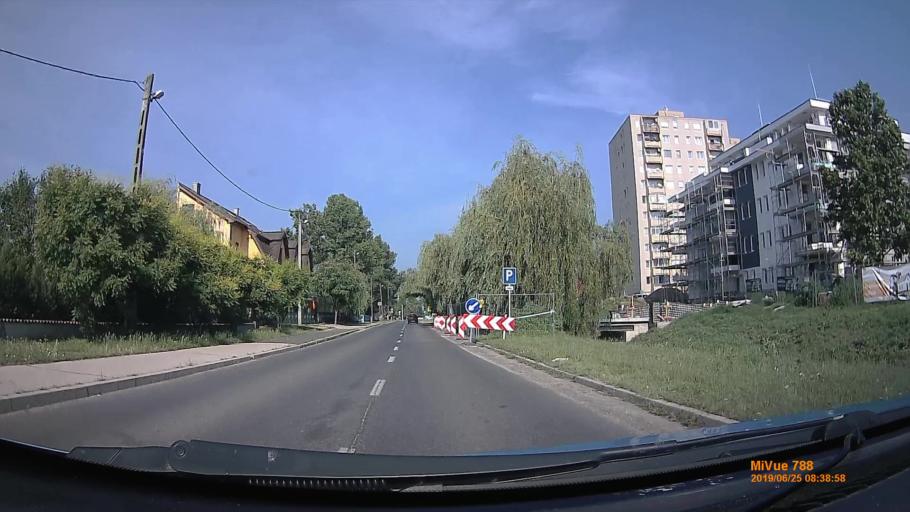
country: HU
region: Fejer
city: Szekesfehervar
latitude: 47.1841
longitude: 18.4048
